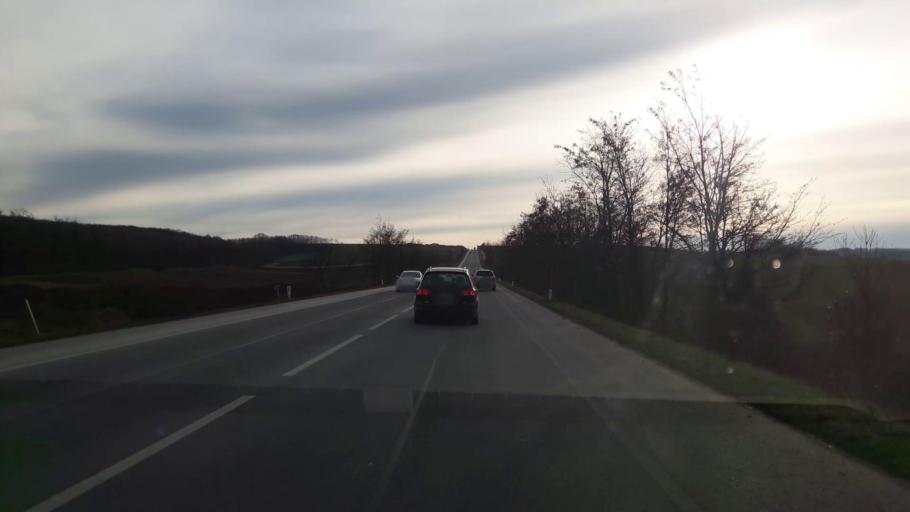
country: AT
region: Lower Austria
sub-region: Politischer Bezirk Mistelbach
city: Drasenhofen
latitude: 48.7260
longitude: 16.6573
